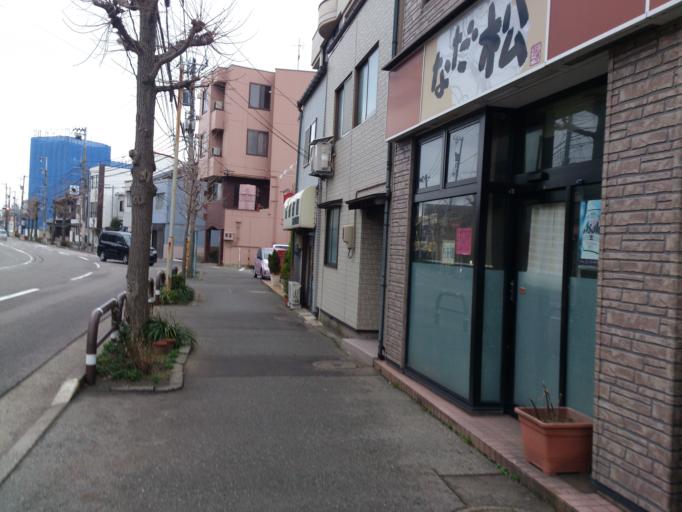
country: JP
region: Ishikawa
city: Kanazawa-shi
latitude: 36.5640
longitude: 136.6482
